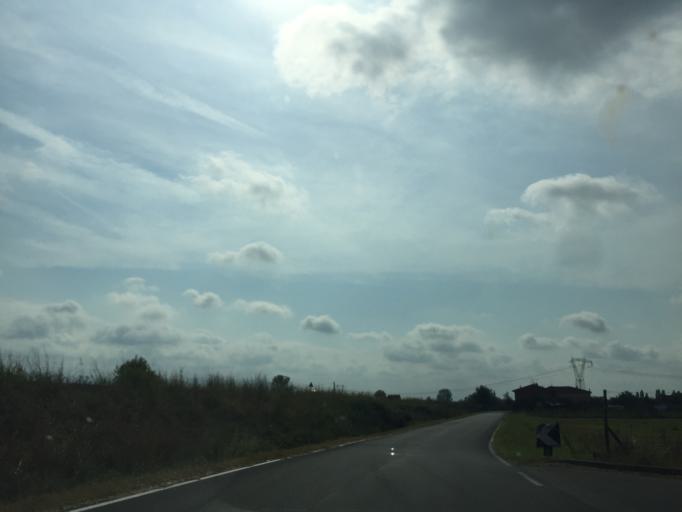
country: IT
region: Tuscany
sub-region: Provincia di Pistoia
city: Cintolese
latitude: 43.8445
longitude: 10.8153
